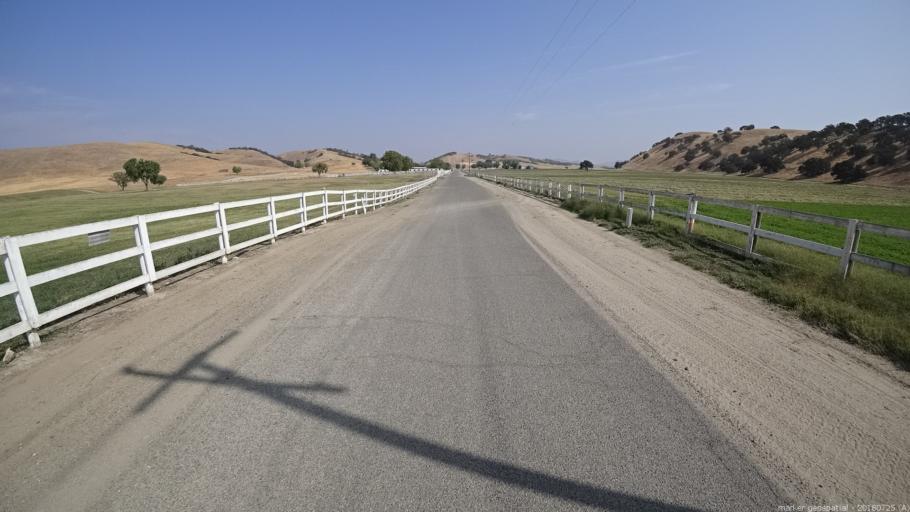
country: US
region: California
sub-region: San Luis Obispo County
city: San Miguel
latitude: 35.8279
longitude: -120.6554
